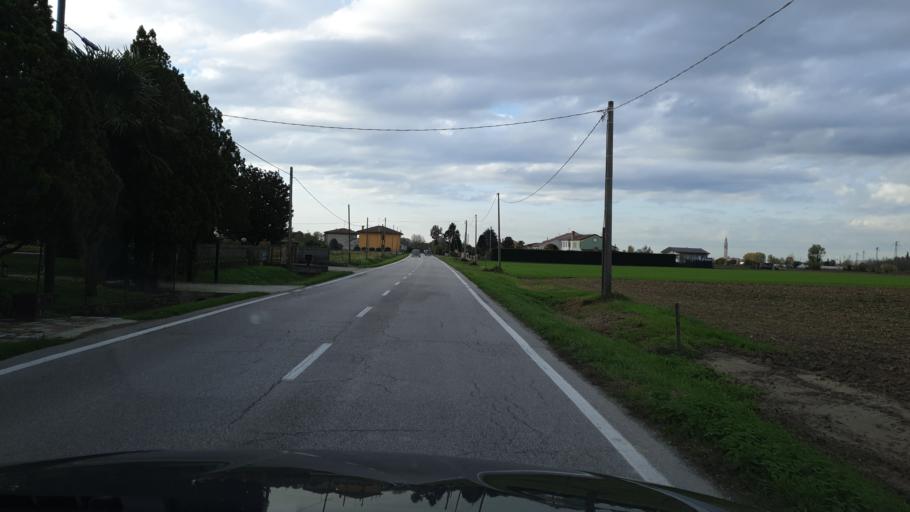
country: IT
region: Veneto
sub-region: Provincia di Rovigo
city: Villanova del Ghebbo Canton
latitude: 45.0699
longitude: 11.6267
